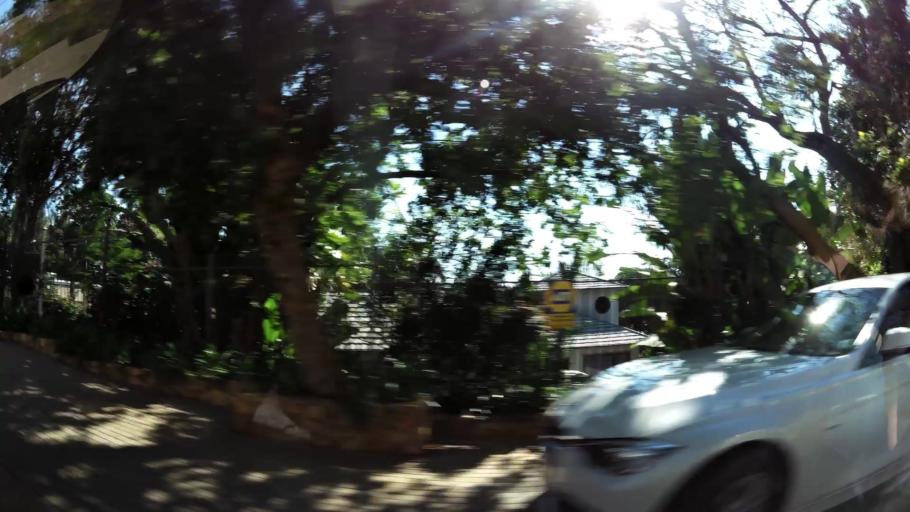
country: ZA
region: Gauteng
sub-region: City of Tshwane Metropolitan Municipality
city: Pretoria
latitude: -25.6893
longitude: 28.2242
